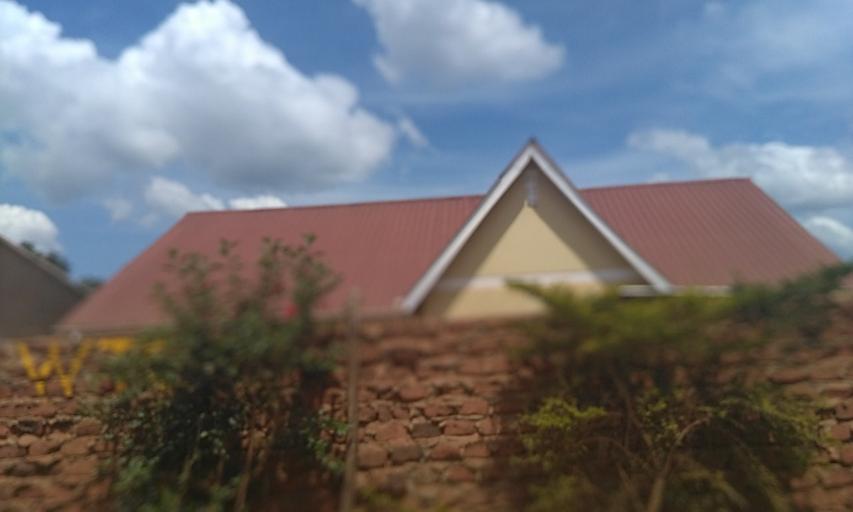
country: UG
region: Central Region
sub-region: Wakiso District
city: Wakiso
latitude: 0.3944
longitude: 32.4619
